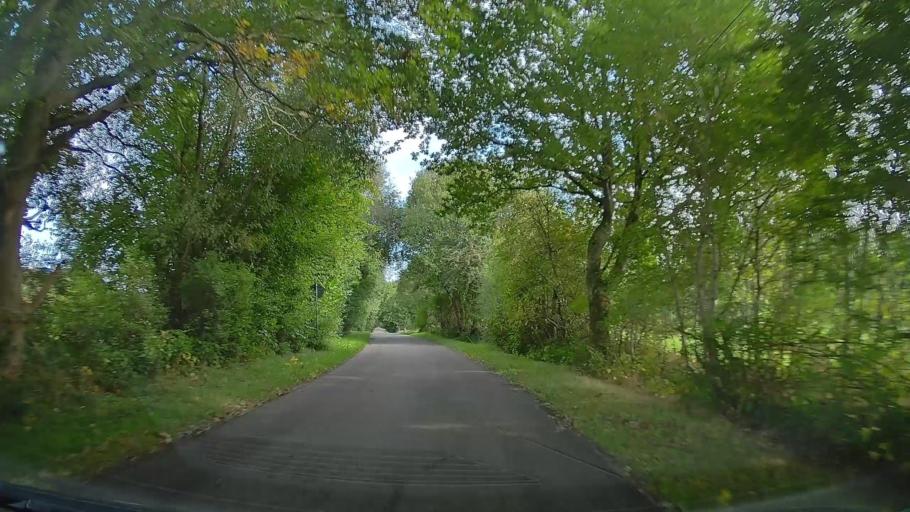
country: DE
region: Schleswig-Holstein
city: Ringsberg
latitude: 54.8314
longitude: 9.5898
